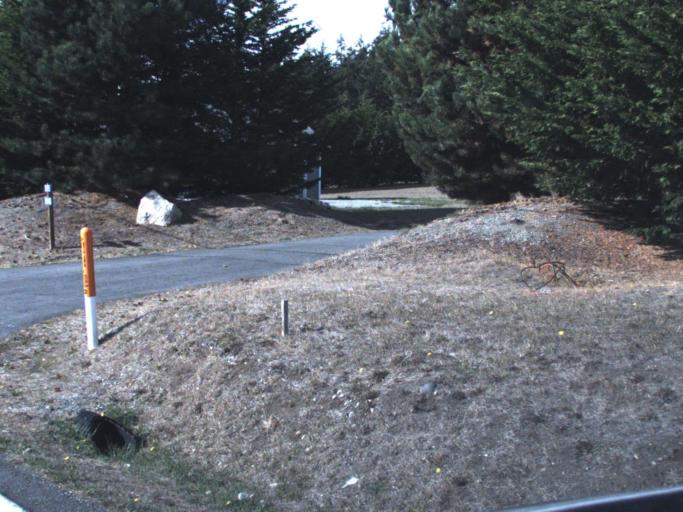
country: US
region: Washington
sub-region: Island County
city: Coupeville
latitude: 48.1709
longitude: -122.6346
